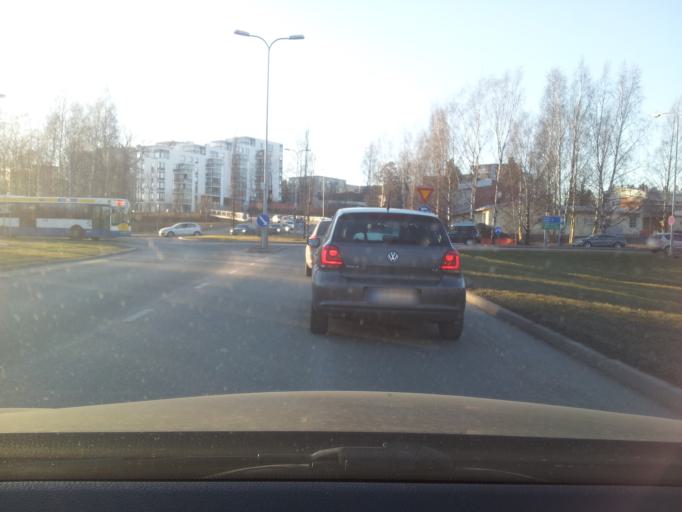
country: FI
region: Uusimaa
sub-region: Helsinki
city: Koukkuniemi
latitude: 60.1616
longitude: 24.7514
